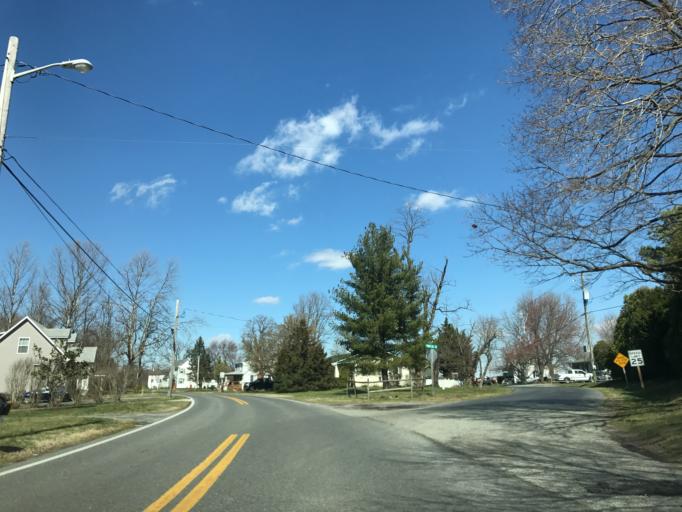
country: US
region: Maryland
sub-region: Queen Anne's County
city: Kingstown
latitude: 39.1490
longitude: -75.9787
